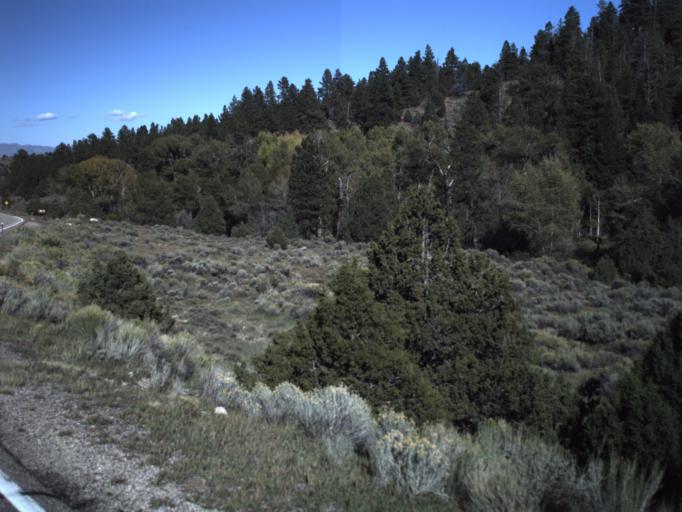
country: US
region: Utah
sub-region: Garfield County
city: Panguitch
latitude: 37.7432
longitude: -112.5900
